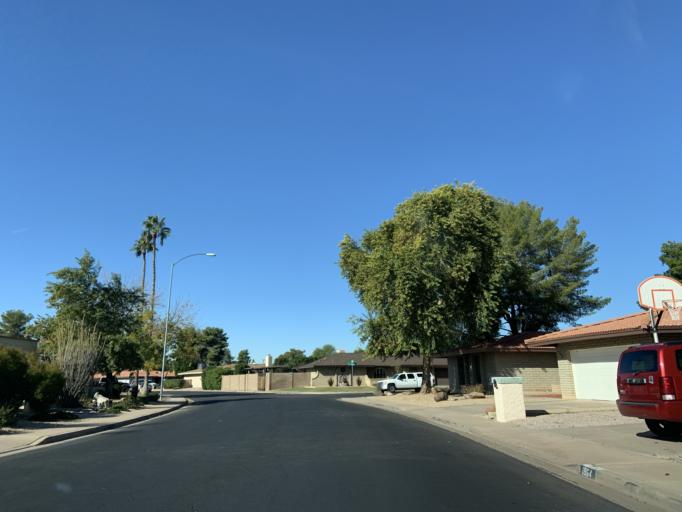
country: US
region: Arizona
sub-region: Maricopa County
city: San Carlos
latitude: 33.3668
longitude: -111.8754
